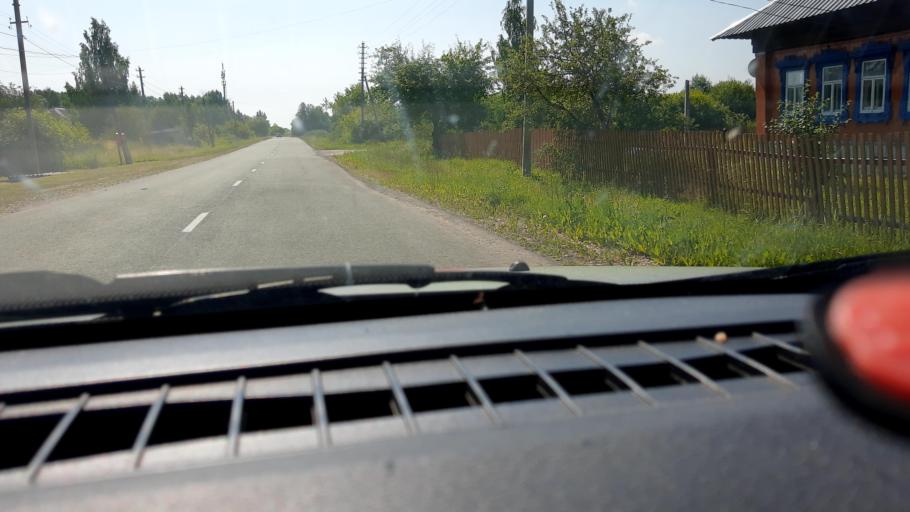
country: RU
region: Nizjnij Novgorod
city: Sharanga
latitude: 57.0475
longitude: 46.5499
